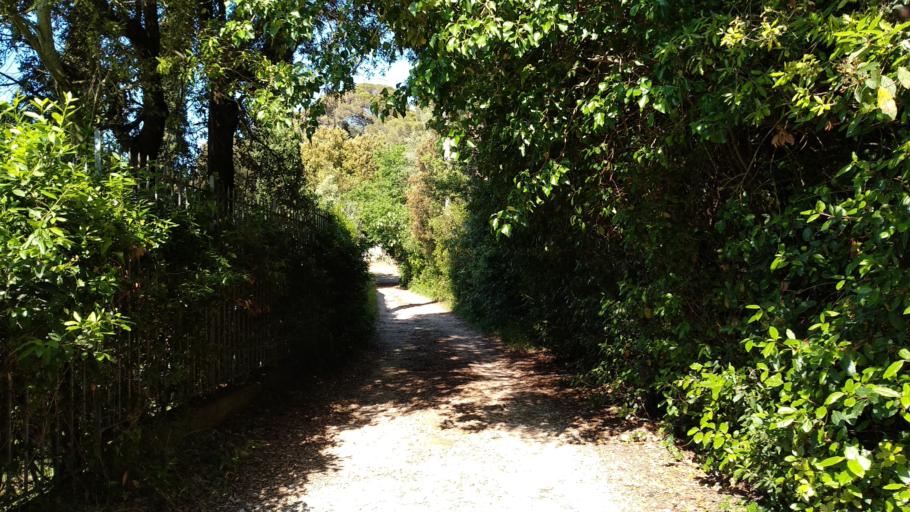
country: IT
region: Tuscany
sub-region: Provincia di Livorno
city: Quercianella
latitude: 43.4945
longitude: 10.3422
